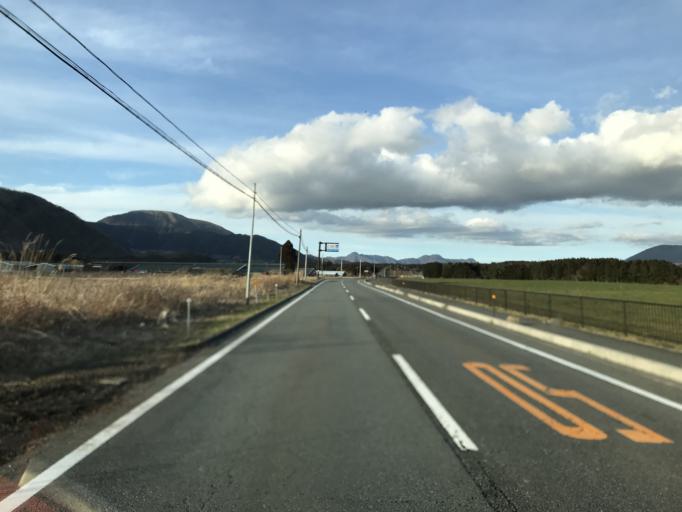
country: JP
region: Yamanashi
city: Fujikawaguchiko
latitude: 35.3943
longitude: 138.5774
